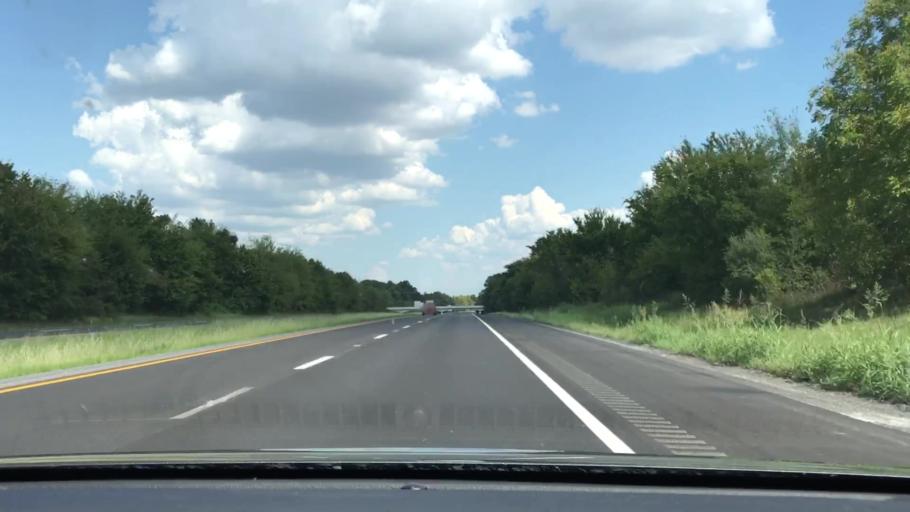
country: US
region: Kentucky
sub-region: Lyon County
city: Eddyville
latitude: 37.0770
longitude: -88.0777
